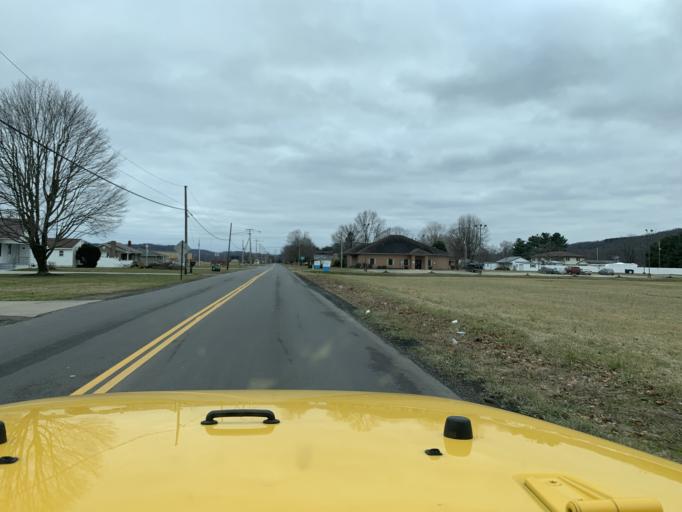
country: US
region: Ohio
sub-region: Tuscarawas County
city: Newcomerstown
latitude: 40.2834
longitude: -81.5671
